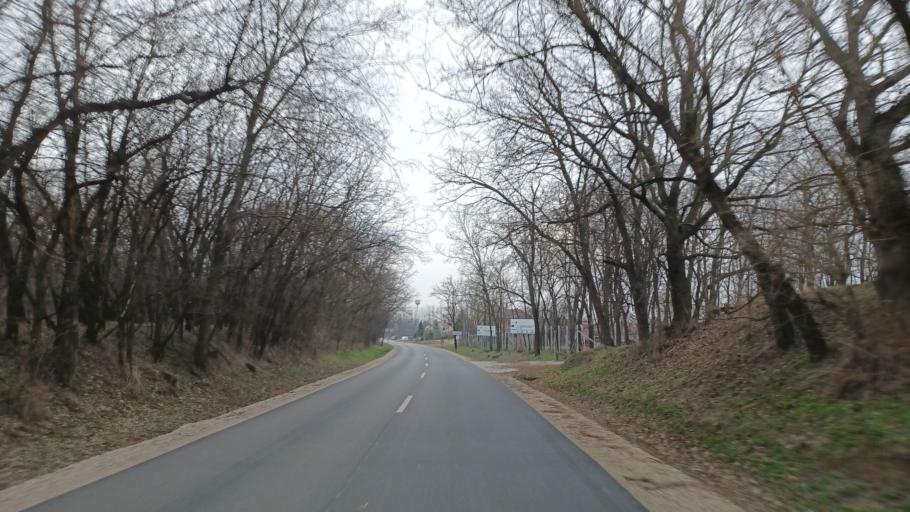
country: HU
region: Tolna
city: Nagydorog
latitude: 46.5723
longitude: 18.6324
